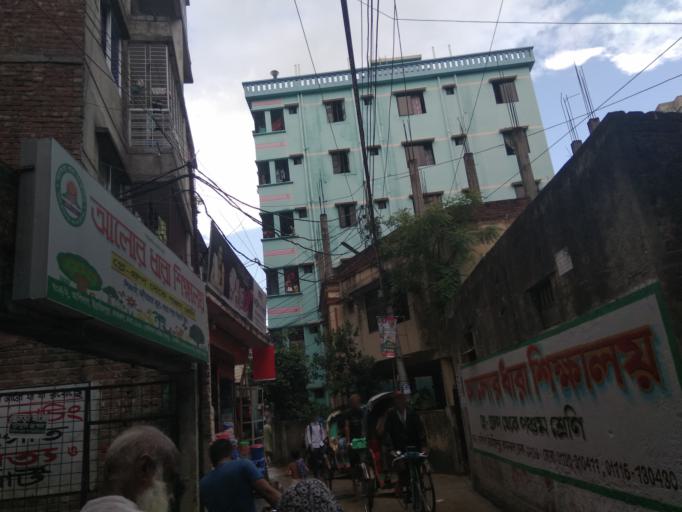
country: BD
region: Dhaka
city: Azimpur
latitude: 23.7984
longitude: 90.3798
